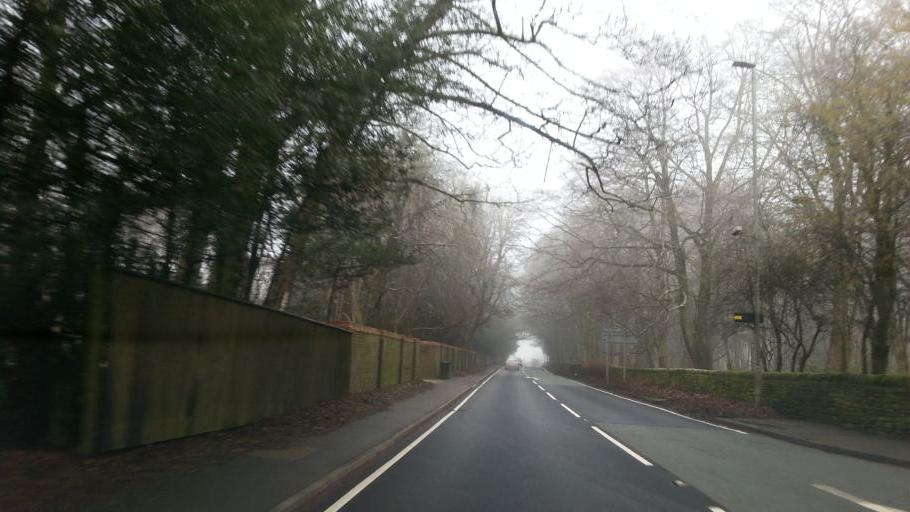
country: GB
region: England
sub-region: Cheshire East
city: Alderley Edge
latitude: 53.2705
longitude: -2.2383
